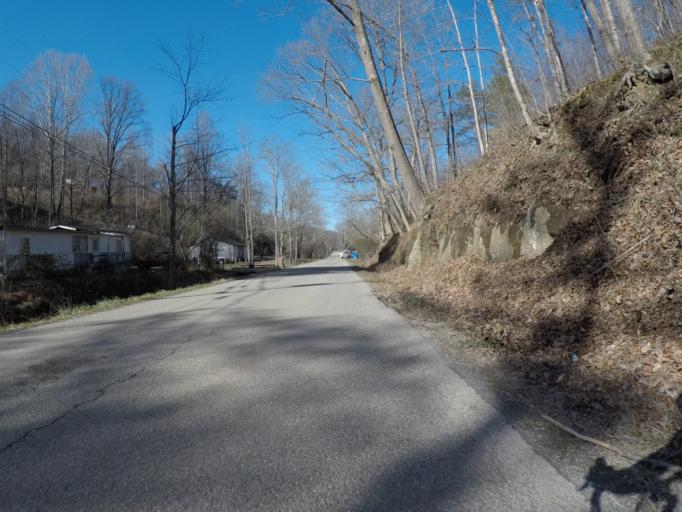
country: US
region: Kentucky
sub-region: Boyd County
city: Catlettsburg
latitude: 38.4077
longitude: -82.6377
